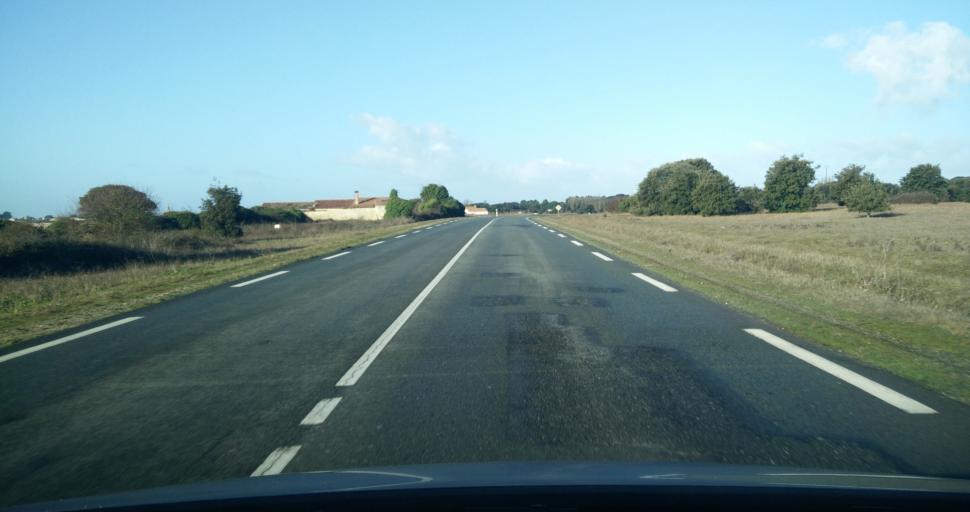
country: FR
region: Poitou-Charentes
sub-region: Departement de la Charente-Maritime
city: Rivedoux-Plage
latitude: 46.1536
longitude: -1.2873
